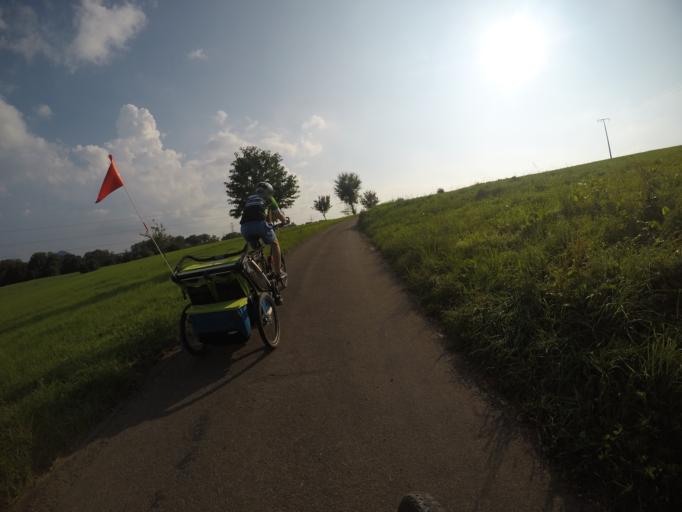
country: DE
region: Baden-Wuerttemberg
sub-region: Tuebingen Region
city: Pliezhausen
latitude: 48.5360
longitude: 9.2232
